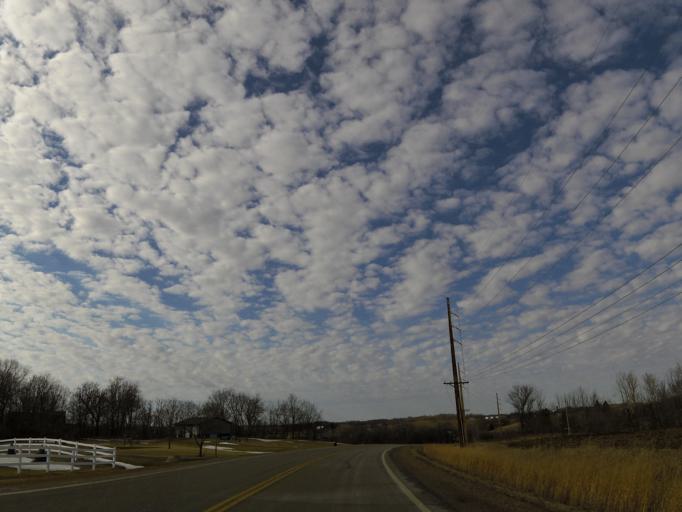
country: US
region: Minnesota
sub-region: Scott County
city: Jordan
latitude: 44.6218
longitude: -93.5616
